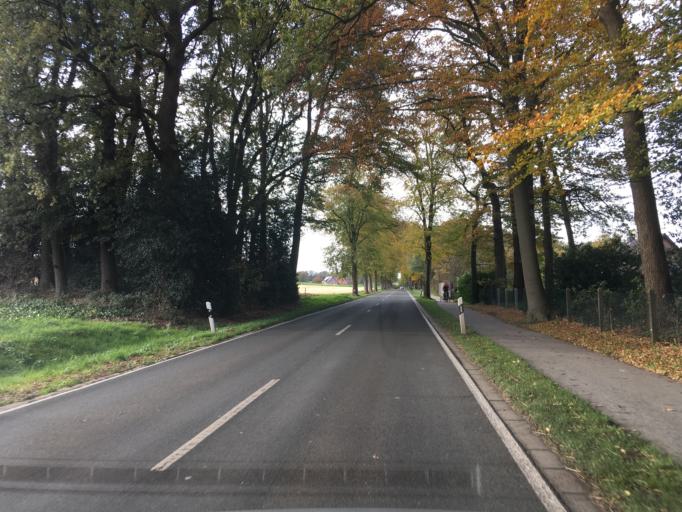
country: DE
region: North Rhine-Westphalia
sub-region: Regierungsbezirk Munster
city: Klein Reken
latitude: 51.8458
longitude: 7.0797
